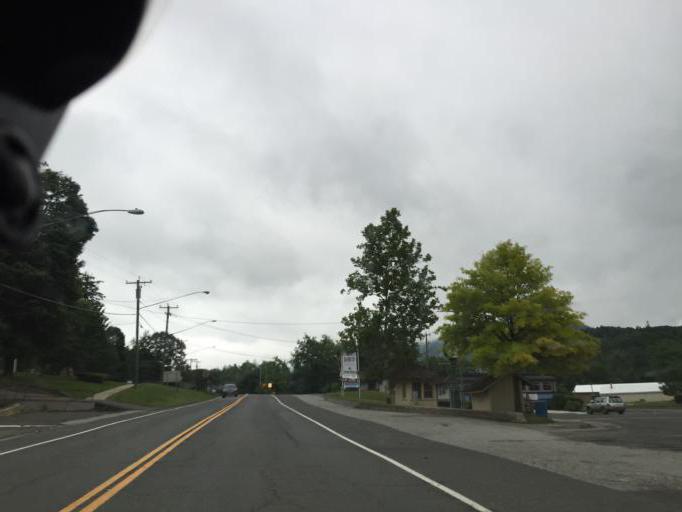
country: US
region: Connecticut
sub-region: Litchfield County
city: Canaan
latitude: 42.0269
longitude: -73.3287
